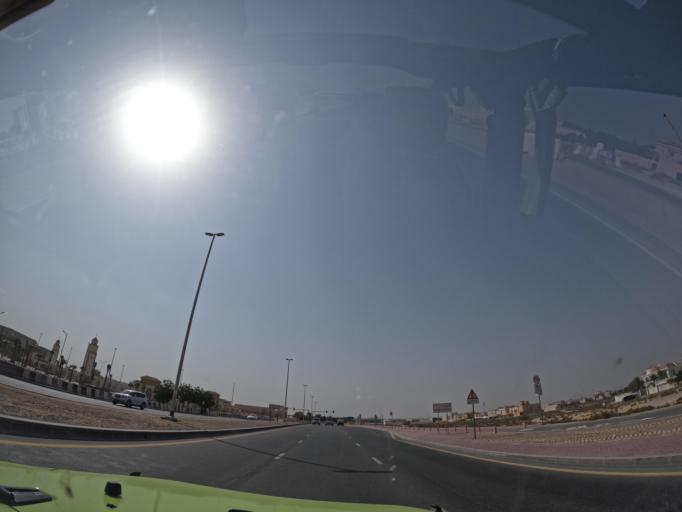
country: AE
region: Ash Shariqah
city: Sharjah
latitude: 25.2006
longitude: 55.4366
